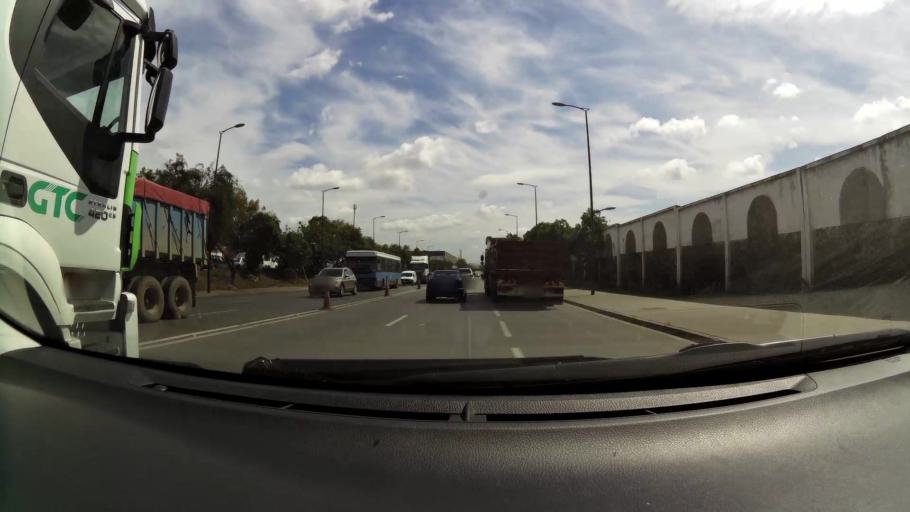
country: MA
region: Grand Casablanca
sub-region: Casablanca
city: Casablanca
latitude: 33.6006
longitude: -7.5611
